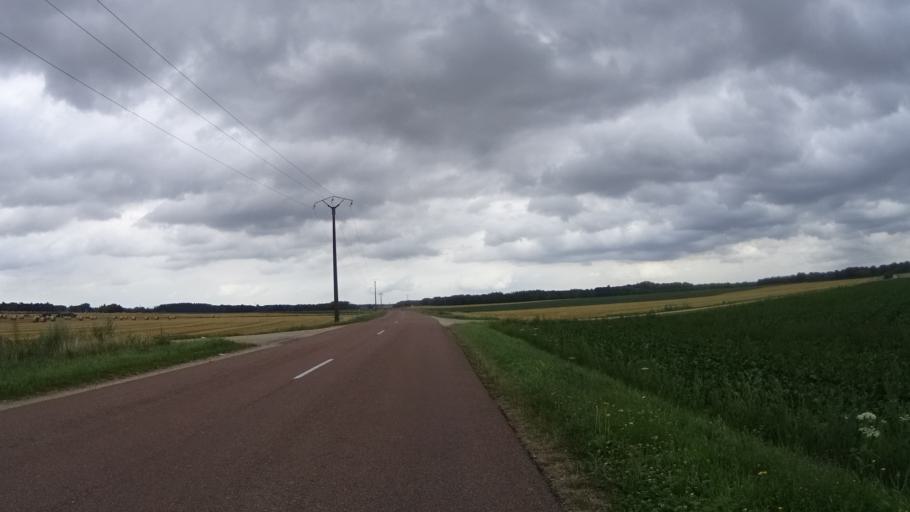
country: FR
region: Champagne-Ardenne
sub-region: Departement de l'Aube
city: Verrieres
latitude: 48.2364
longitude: 4.1597
